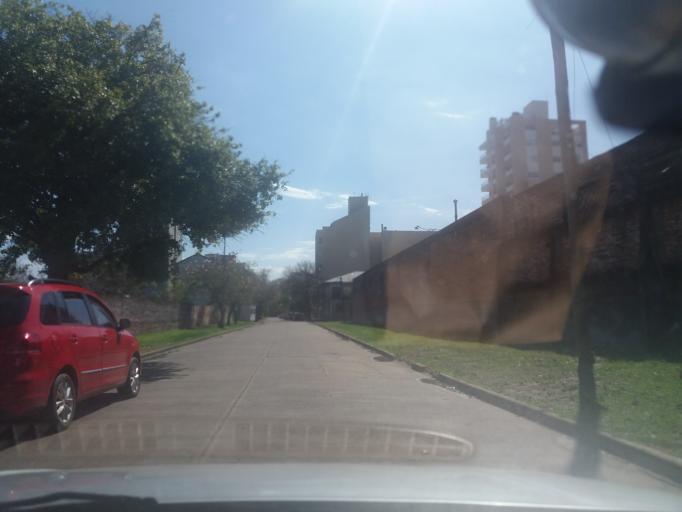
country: AR
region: Corrientes
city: Corrientes
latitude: -27.4729
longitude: -58.8512
